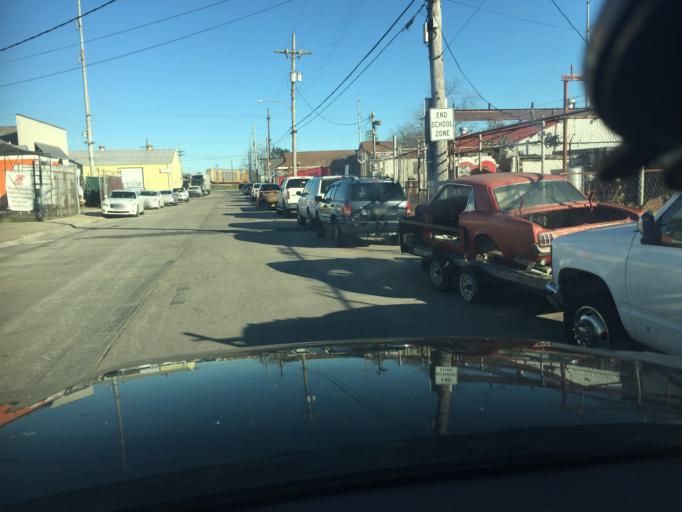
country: US
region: Louisiana
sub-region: Orleans Parish
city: New Orleans
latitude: 29.9873
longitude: -90.0663
